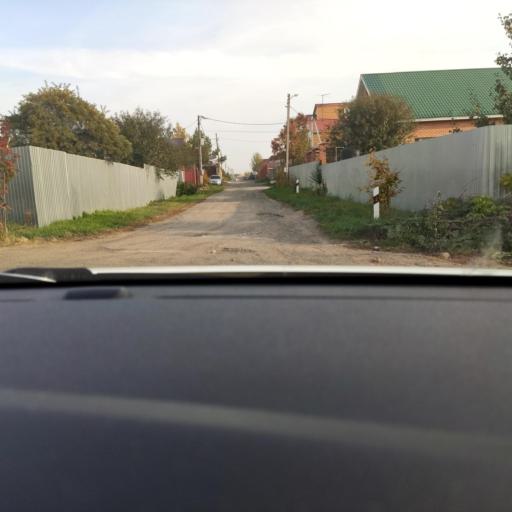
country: RU
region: Tatarstan
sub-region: Gorod Kazan'
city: Kazan
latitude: 55.8236
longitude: 49.2229
